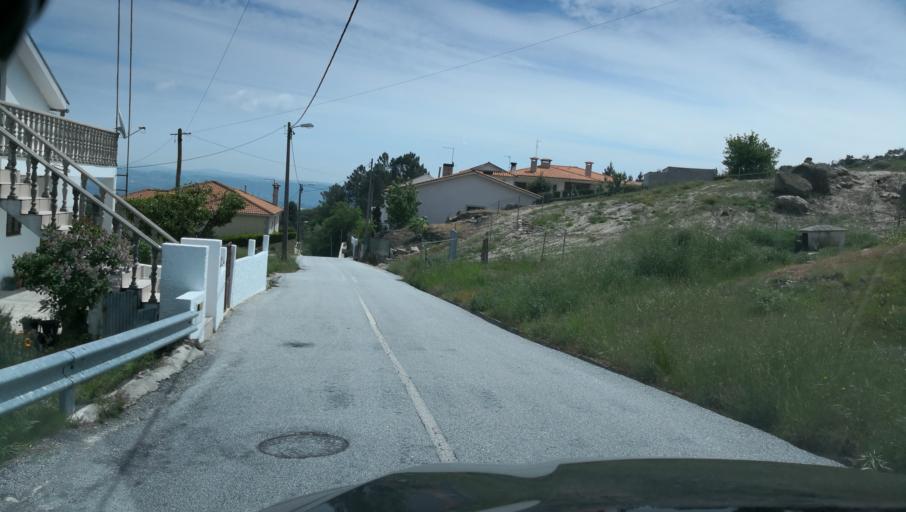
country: PT
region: Vila Real
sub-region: Vila Real
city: Vila Real
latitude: 41.3137
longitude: -7.7863
